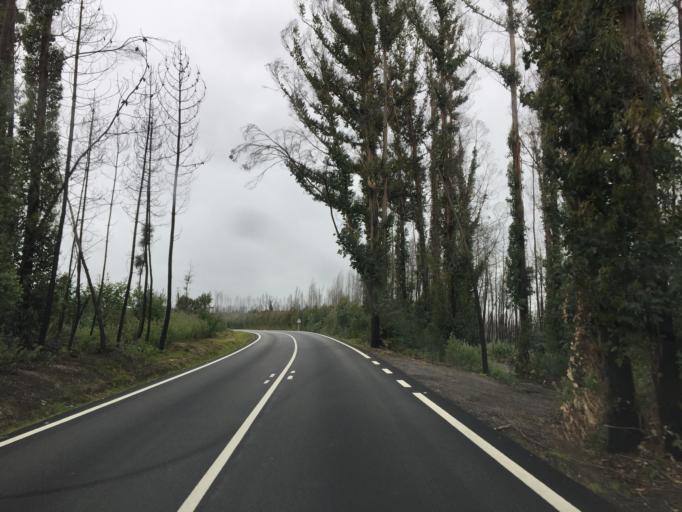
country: PT
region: Coimbra
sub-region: Tabua
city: Tabua
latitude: 40.3277
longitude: -7.9542
